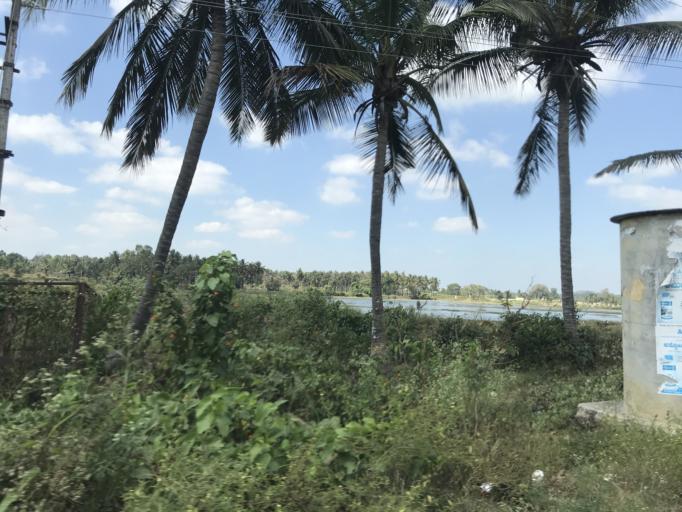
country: IN
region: Karnataka
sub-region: Mysore
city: Hunsur
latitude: 12.2919
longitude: 76.2896
